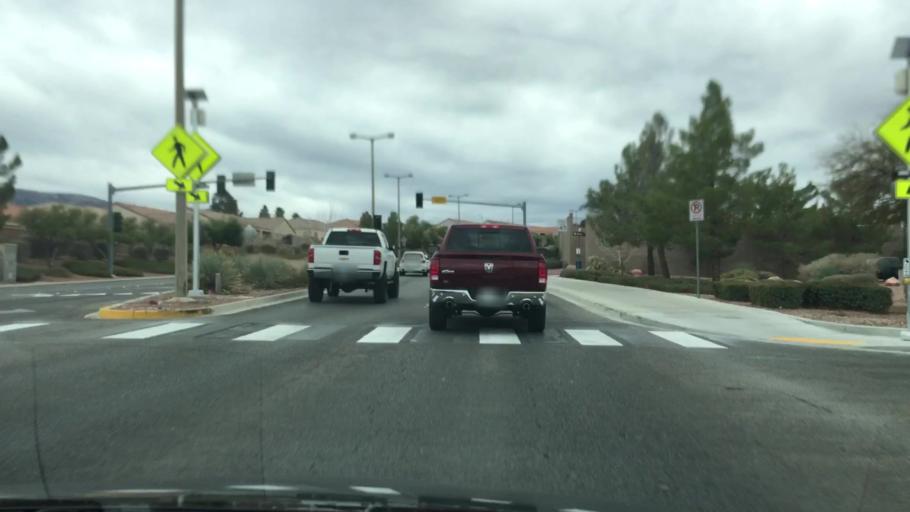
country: US
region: Nevada
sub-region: Clark County
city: Whitney
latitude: 35.9521
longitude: -115.0926
